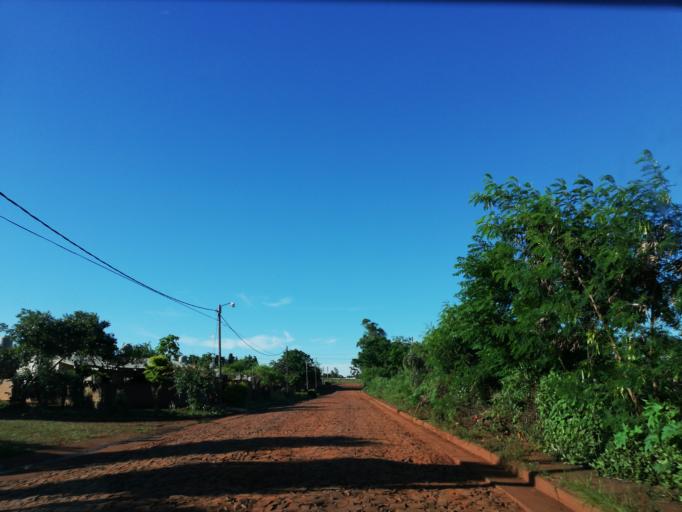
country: AR
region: Misiones
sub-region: Departamento de Capital
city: Posadas
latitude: -27.4357
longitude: -55.9354
